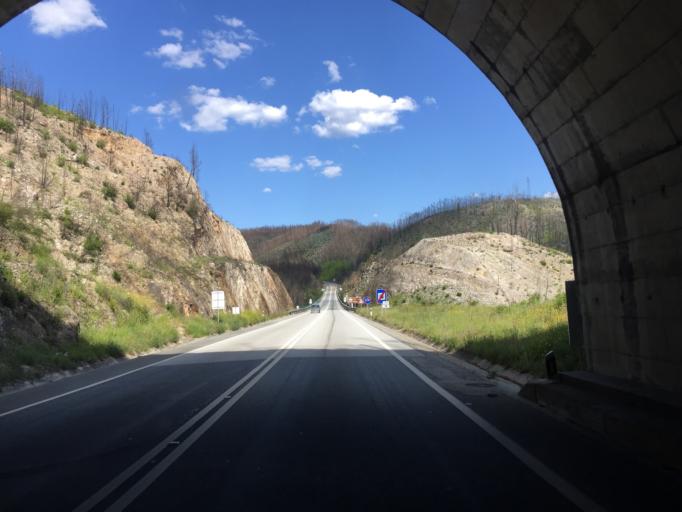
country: PT
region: Leiria
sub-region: Figueiro Dos Vinhos
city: Figueiro dos Vinhos
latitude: 39.9275
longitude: -8.3129
